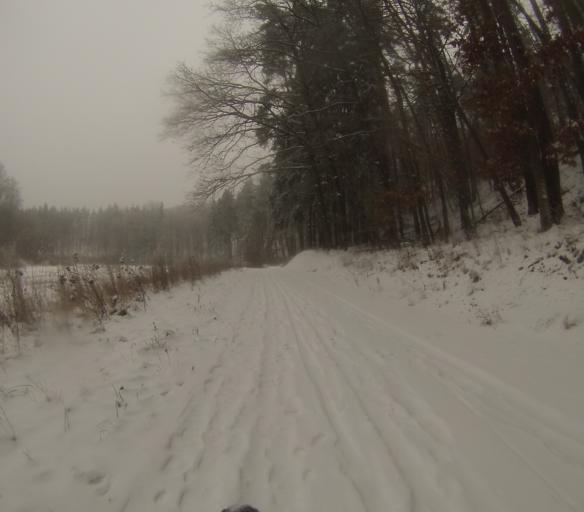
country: CZ
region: South Moravian
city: Strelice
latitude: 49.1358
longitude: 16.4943
